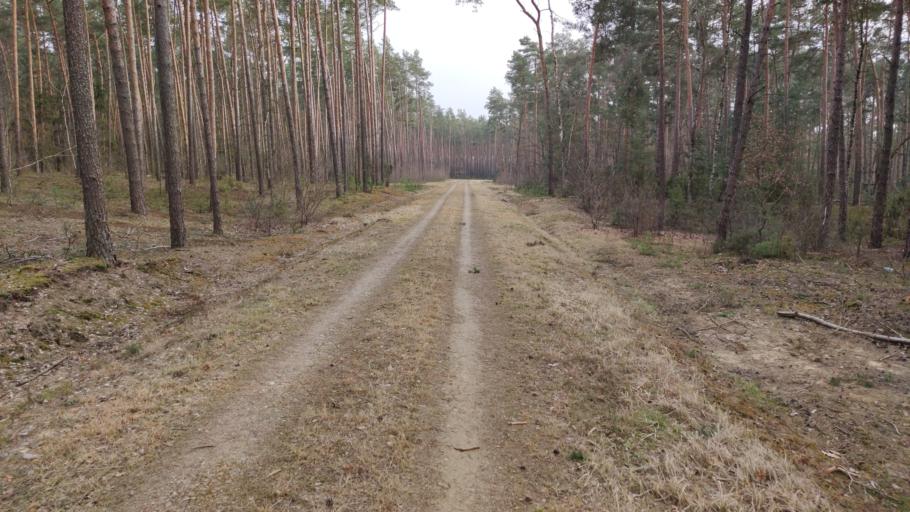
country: PL
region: Masovian Voivodeship
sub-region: Powiat plocki
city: Bodzanow
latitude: 52.4502
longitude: 19.9628
